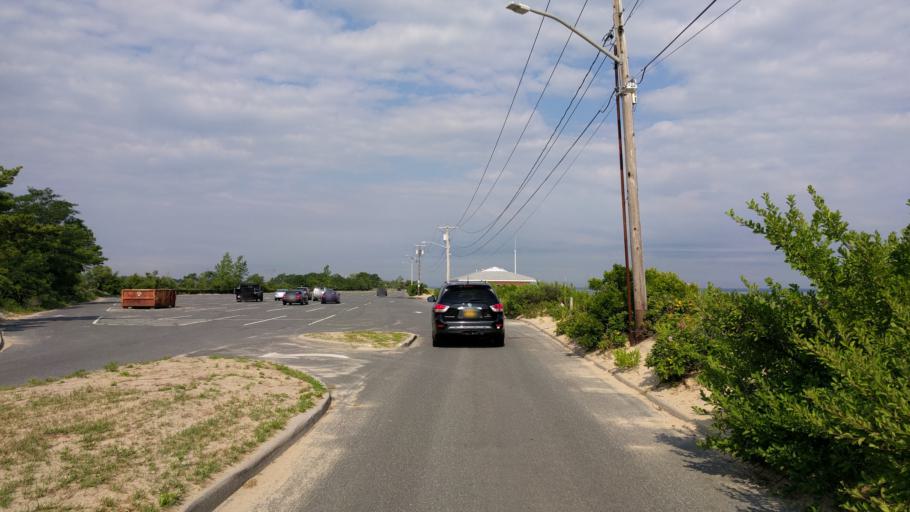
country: US
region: New York
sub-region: Nassau County
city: Lattingtown
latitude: 40.9086
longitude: -73.5859
